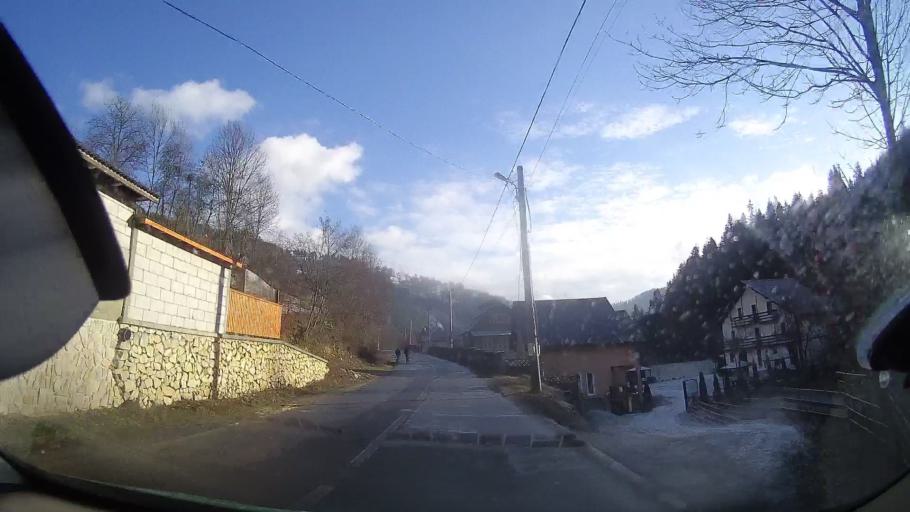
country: RO
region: Alba
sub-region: Comuna Vadu Motilor
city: Vadu Motilor
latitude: 46.3934
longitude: 22.9683
